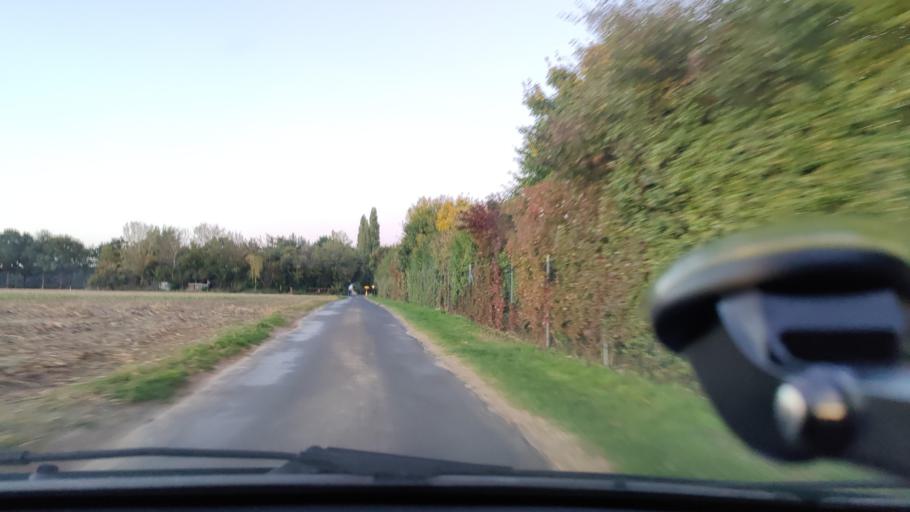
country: DE
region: North Rhine-Westphalia
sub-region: Regierungsbezirk Dusseldorf
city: Goch
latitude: 51.7172
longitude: 6.1809
